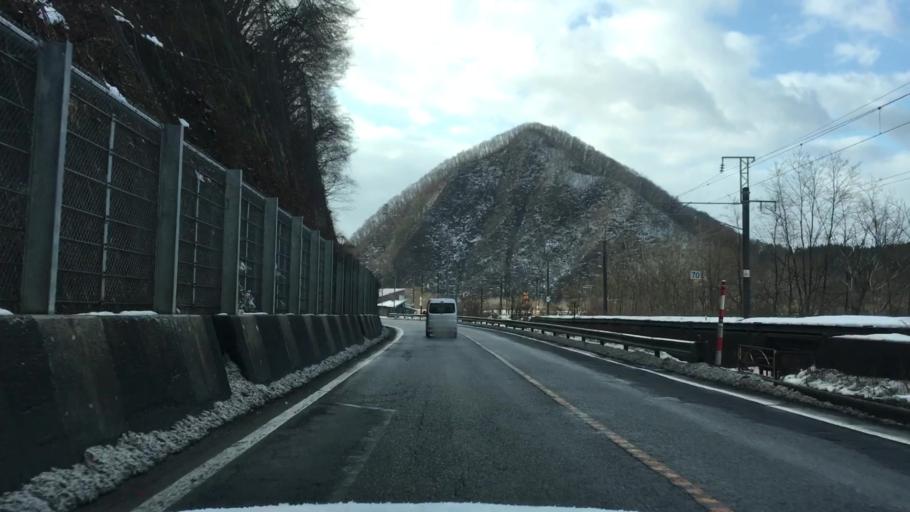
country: JP
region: Akita
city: Odate
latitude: 40.3631
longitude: 140.5972
